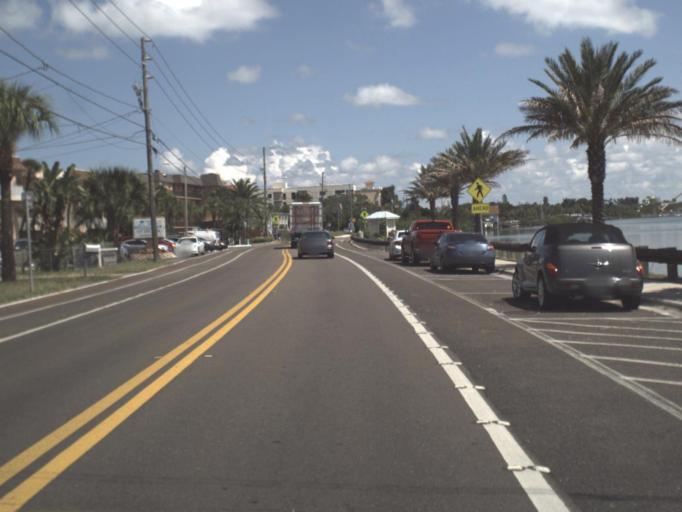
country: US
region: Florida
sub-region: Pinellas County
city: Indian Rocks Beach
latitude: 27.8746
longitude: -82.8501
